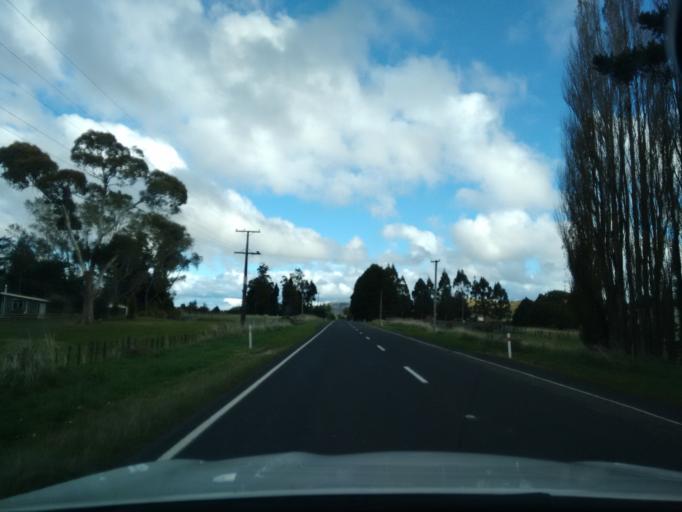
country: NZ
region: Manawatu-Wanganui
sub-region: Ruapehu District
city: Waiouru
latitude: -39.4045
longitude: 175.2852
